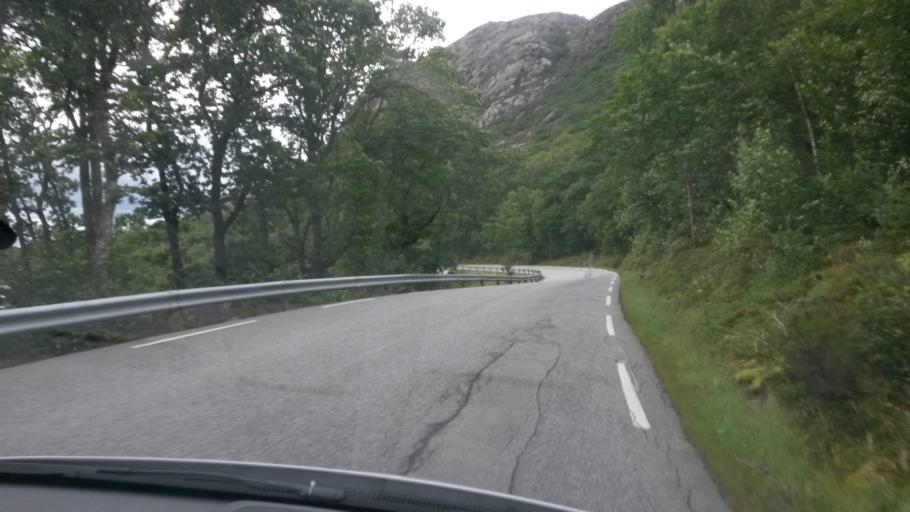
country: NO
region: Rogaland
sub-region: Sandnes
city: Sandnes
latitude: 58.8854
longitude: 5.7760
